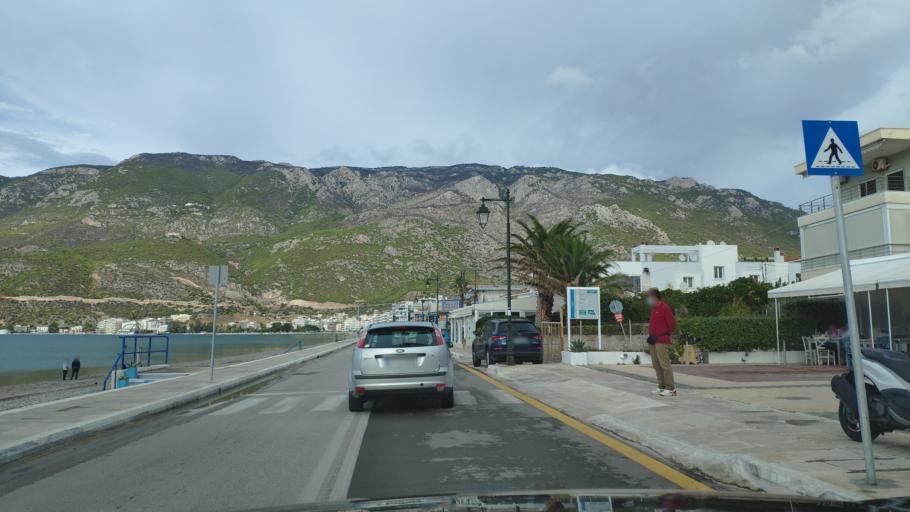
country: GR
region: Peloponnese
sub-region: Nomos Korinthias
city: Loutraki
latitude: 37.9674
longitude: 22.9725
